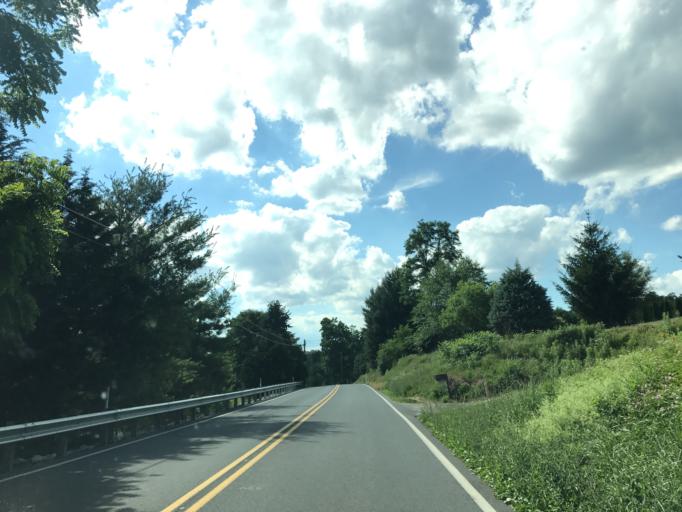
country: US
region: Pennsylvania
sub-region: York County
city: Parkville
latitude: 39.7642
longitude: -76.8587
